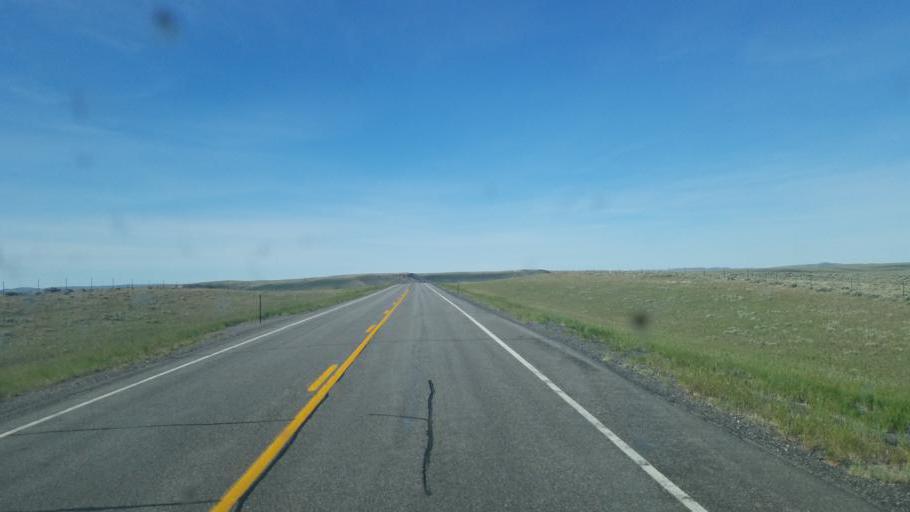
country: US
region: Wyoming
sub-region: Fremont County
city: Riverton
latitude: 42.6326
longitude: -108.1947
